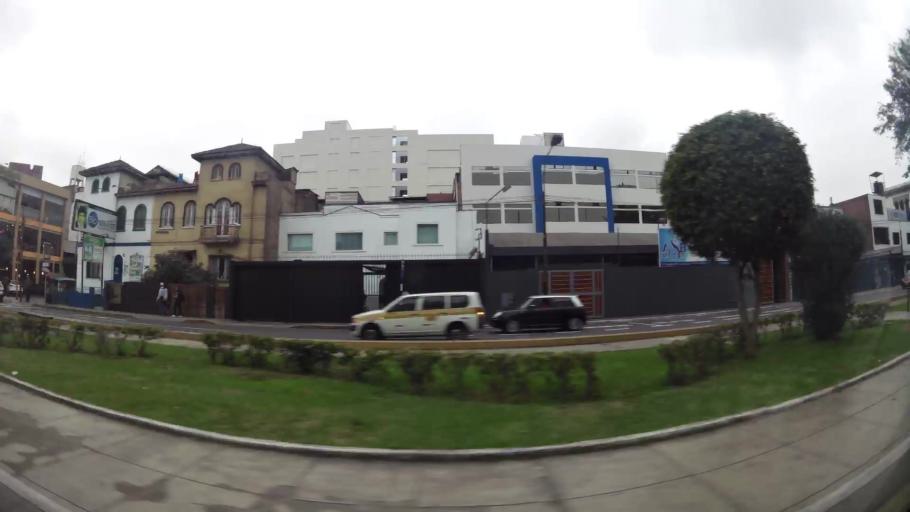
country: PE
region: Lima
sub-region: Lima
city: San Isidro
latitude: -12.0874
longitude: -77.0341
